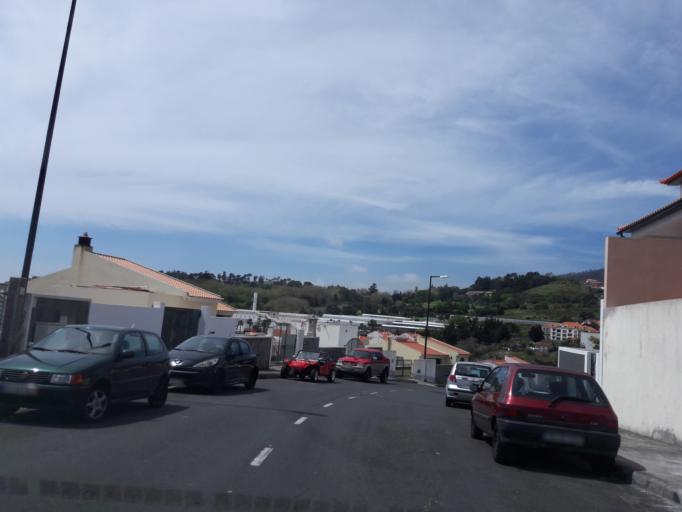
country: PT
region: Madeira
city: Canico
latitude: 32.6538
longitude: -16.8534
